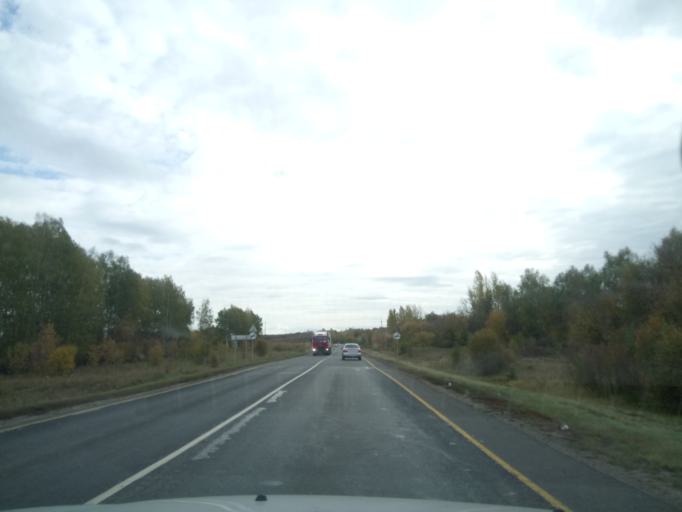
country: RU
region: Nizjnij Novgorod
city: Lukoyanov
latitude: 55.0549
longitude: 44.3703
